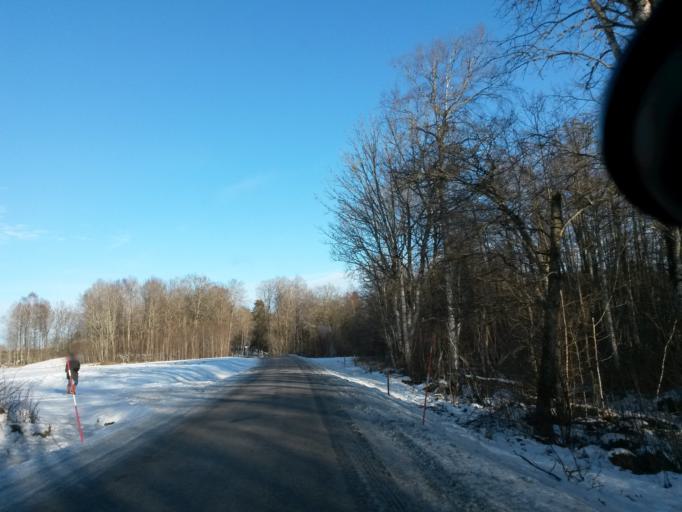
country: SE
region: Vaestra Goetaland
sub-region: Vargarda Kommun
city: Vargarda
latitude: 58.0302
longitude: 12.8586
